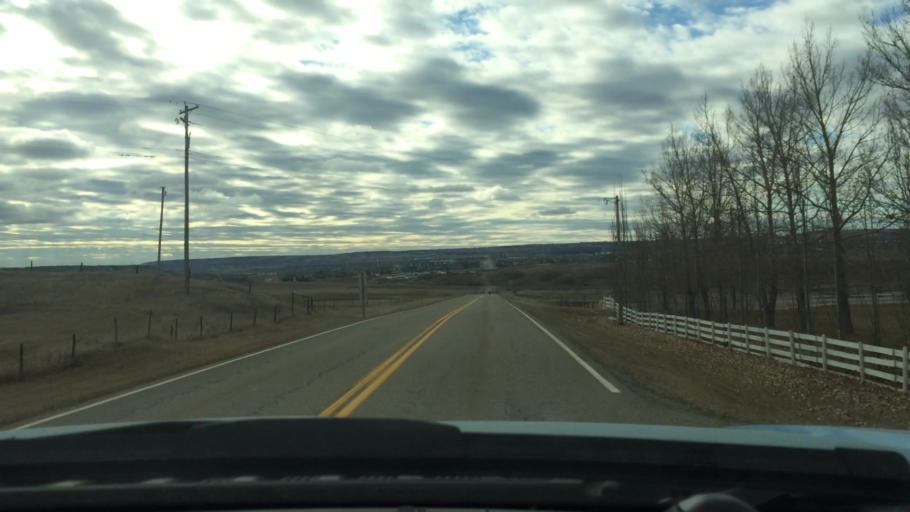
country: CA
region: Alberta
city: Airdrie
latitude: 51.1984
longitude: -114.1412
